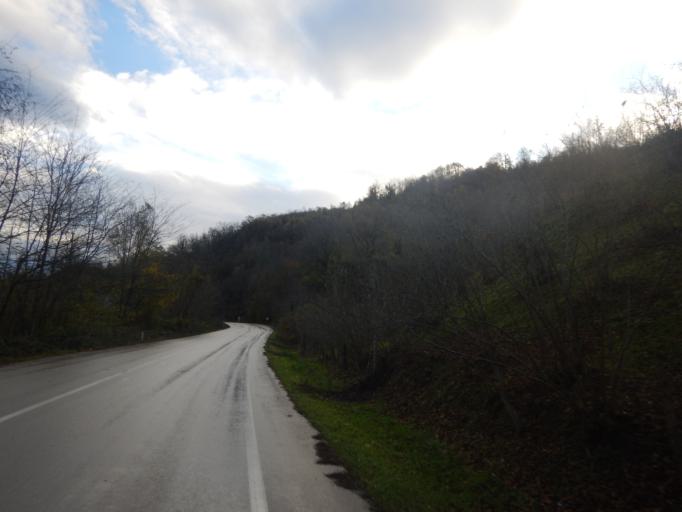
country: TR
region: Ordu
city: Kumru
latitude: 40.9044
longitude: 37.3253
